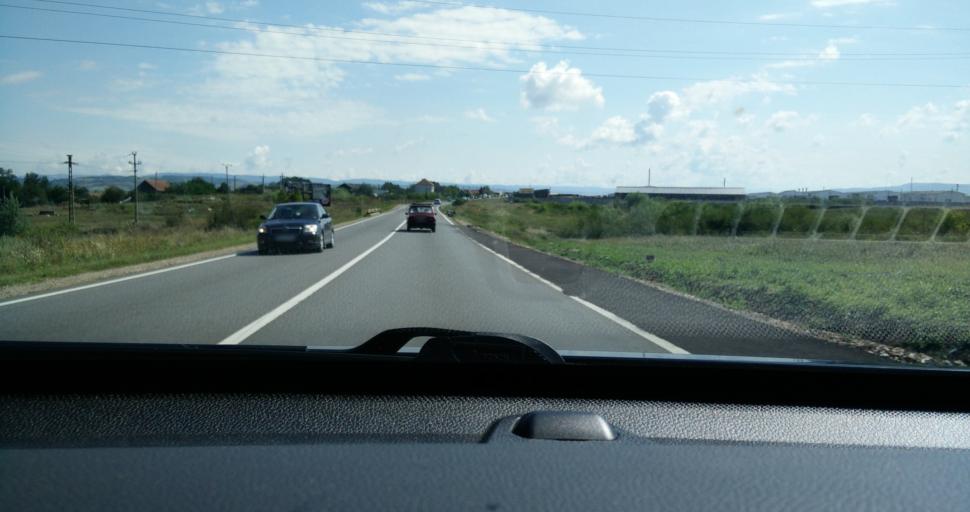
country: RO
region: Bihor
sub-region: Comuna Sacadat
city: Sacadat
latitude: 47.0612
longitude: 22.1462
